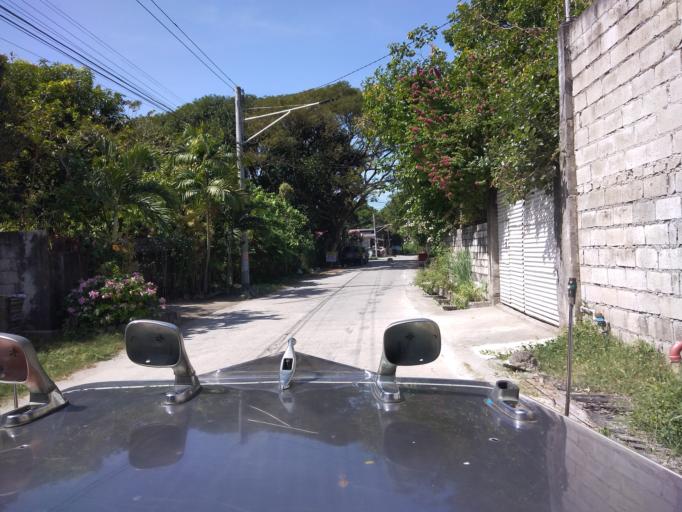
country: PH
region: Central Luzon
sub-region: Province of Pampanga
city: Bacolor
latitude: 15.0067
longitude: 120.6608
